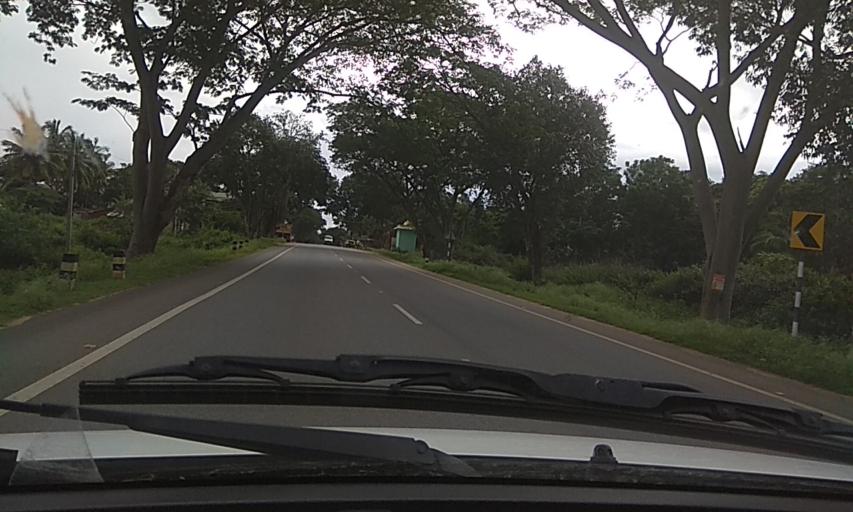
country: IN
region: Karnataka
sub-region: Tumkur
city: Kunigal
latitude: 13.1292
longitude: 77.0288
